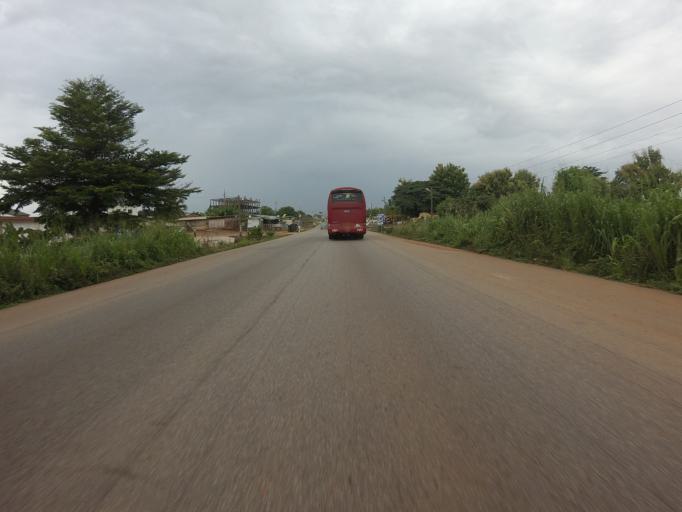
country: GH
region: Ashanti
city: Konongo
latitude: 6.6189
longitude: -1.1916
